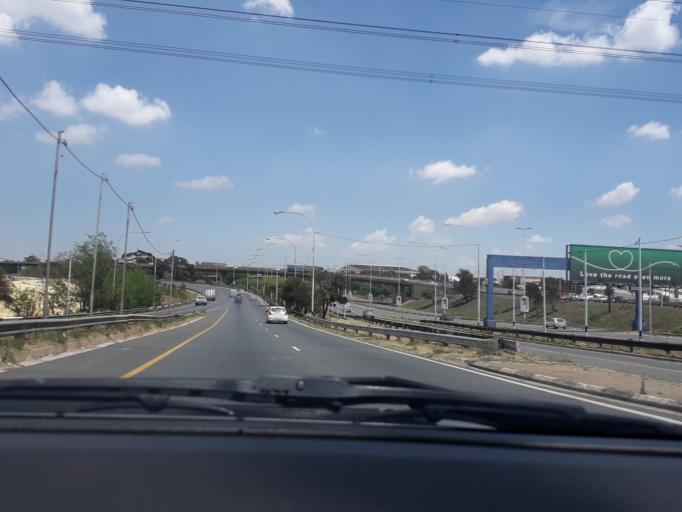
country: ZA
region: Gauteng
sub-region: City of Johannesburg Metropolitan Municipality
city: Johannesburg
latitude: -26.2127
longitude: 28.0278
